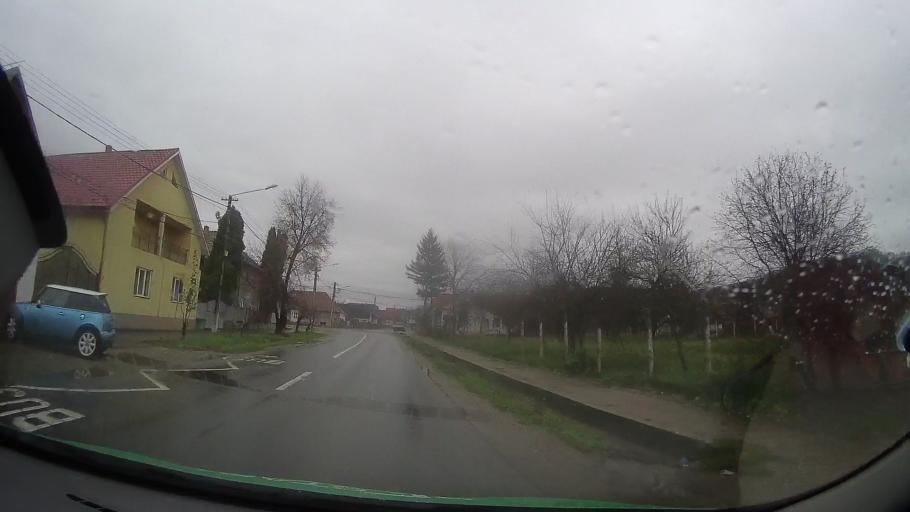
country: RO
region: Bistrita-Nasaud
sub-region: Municipiul Bistrita
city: Viisoara
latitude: 47.0778
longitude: 24.4378
